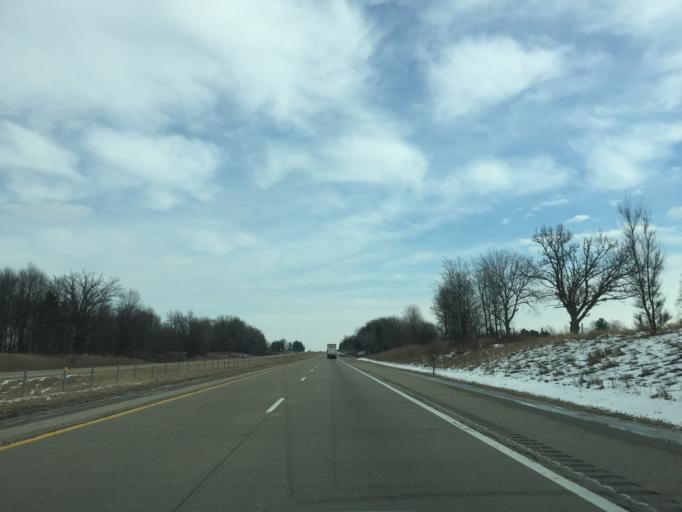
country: US
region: Michigan
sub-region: Ionia County
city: Saranac
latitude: 42.8791
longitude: -85.2633
